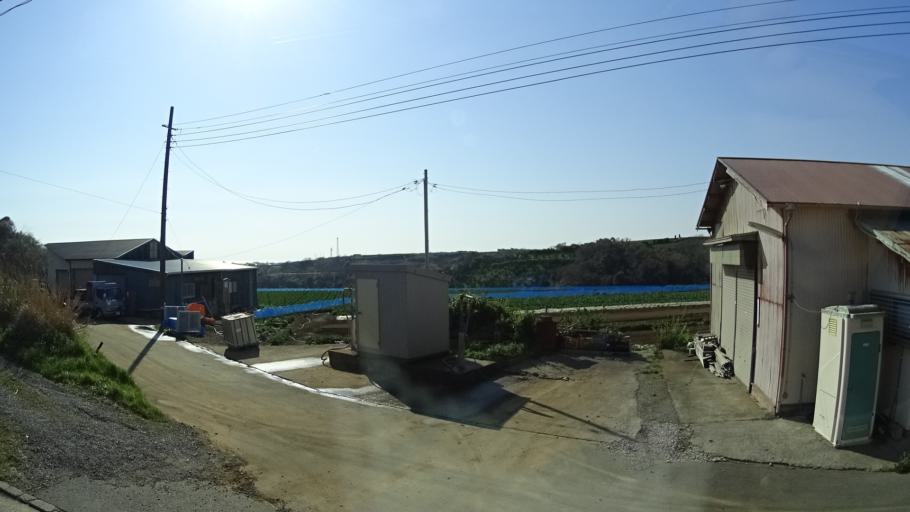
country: JP
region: Kanagawa
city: Miura
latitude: 35.1534
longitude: 139.6458
